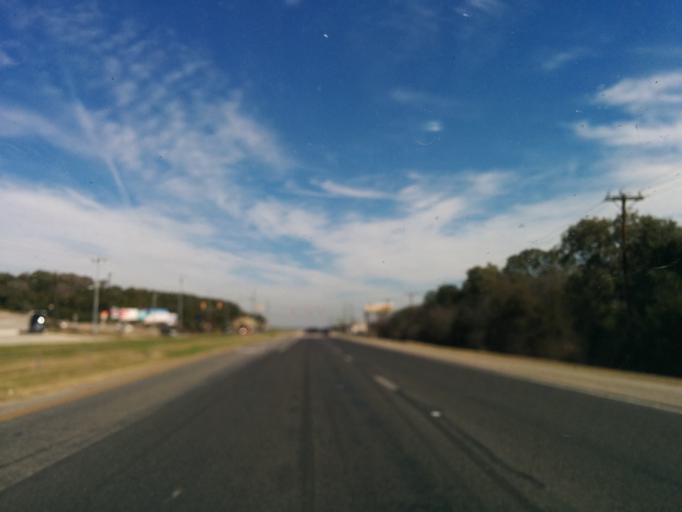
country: US
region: Texas
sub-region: Bexar County
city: Timberwood Park
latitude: 29.7086
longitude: -98.4494
